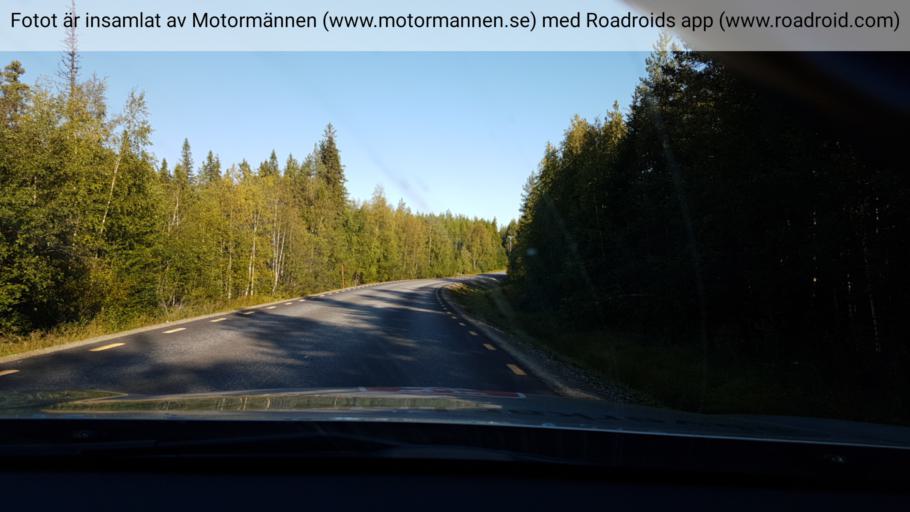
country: SE
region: Vaesterbotten
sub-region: Vindelns Kommun
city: Vindeln
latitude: 64.4562
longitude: 19.3330
